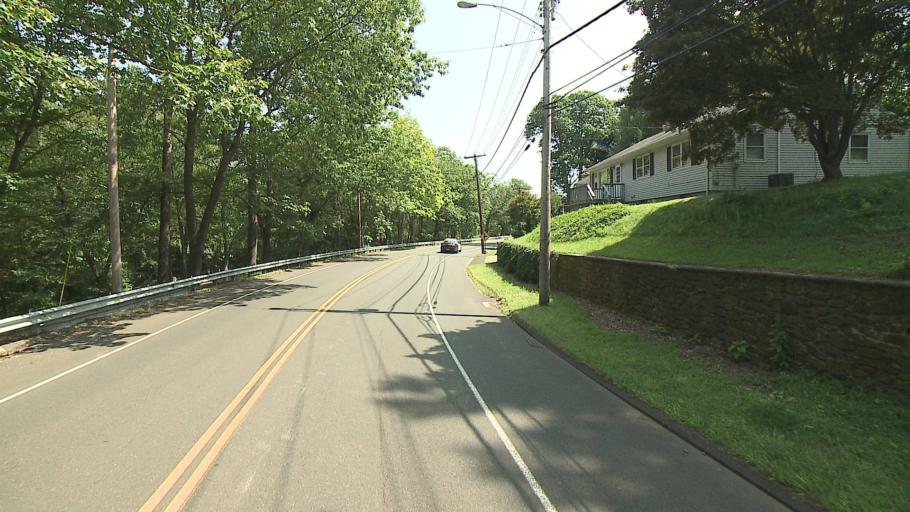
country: US
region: Connecticut
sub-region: Fairfield County
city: Shelton
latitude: 41.3243
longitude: -73.1046
